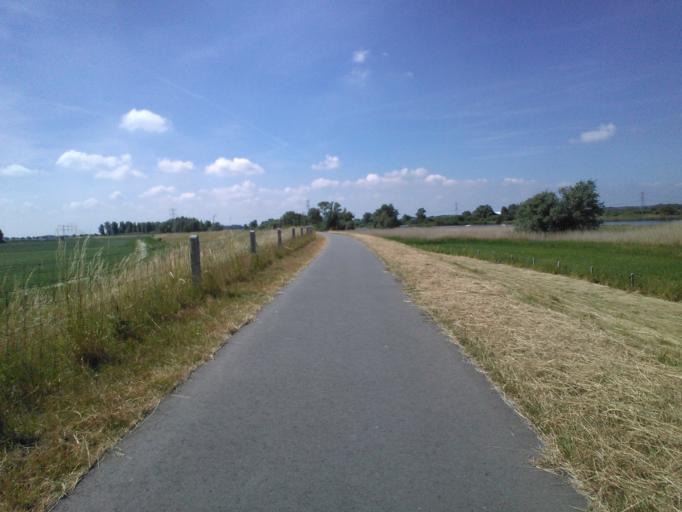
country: NL
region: North Brabant
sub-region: Gemeente Werkendam
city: Werkendam
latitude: 51.7720
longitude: 4.8636
